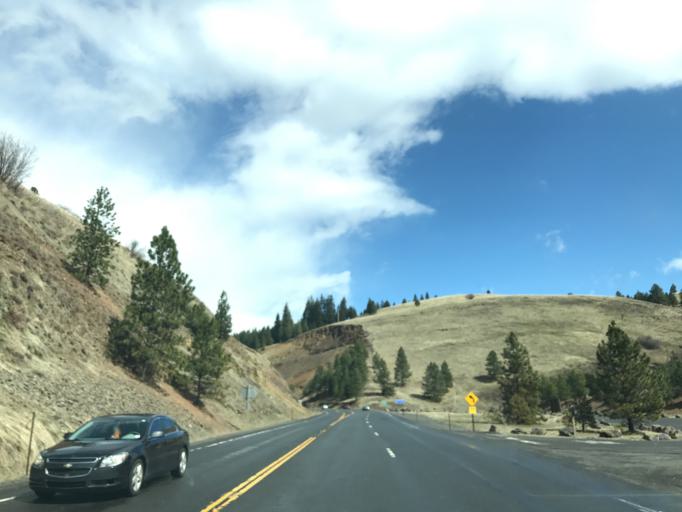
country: US
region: Idaho
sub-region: Idaho County
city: Grangeville
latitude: 45.8390
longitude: -116.2382
